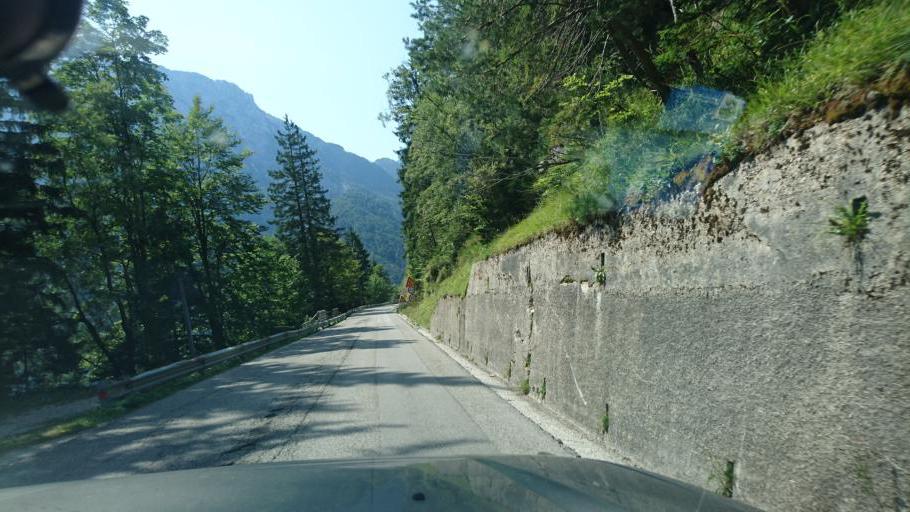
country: SI
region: Bovec
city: Bovec
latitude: 46.4228
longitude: 13.5633
